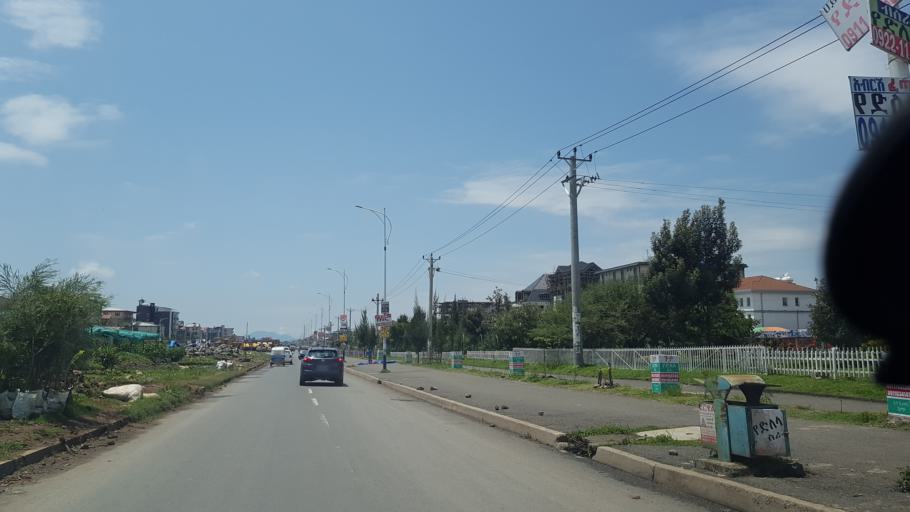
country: ET
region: Adis Abeba
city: Addis Ababa
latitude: 9.0183
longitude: 38.8521
